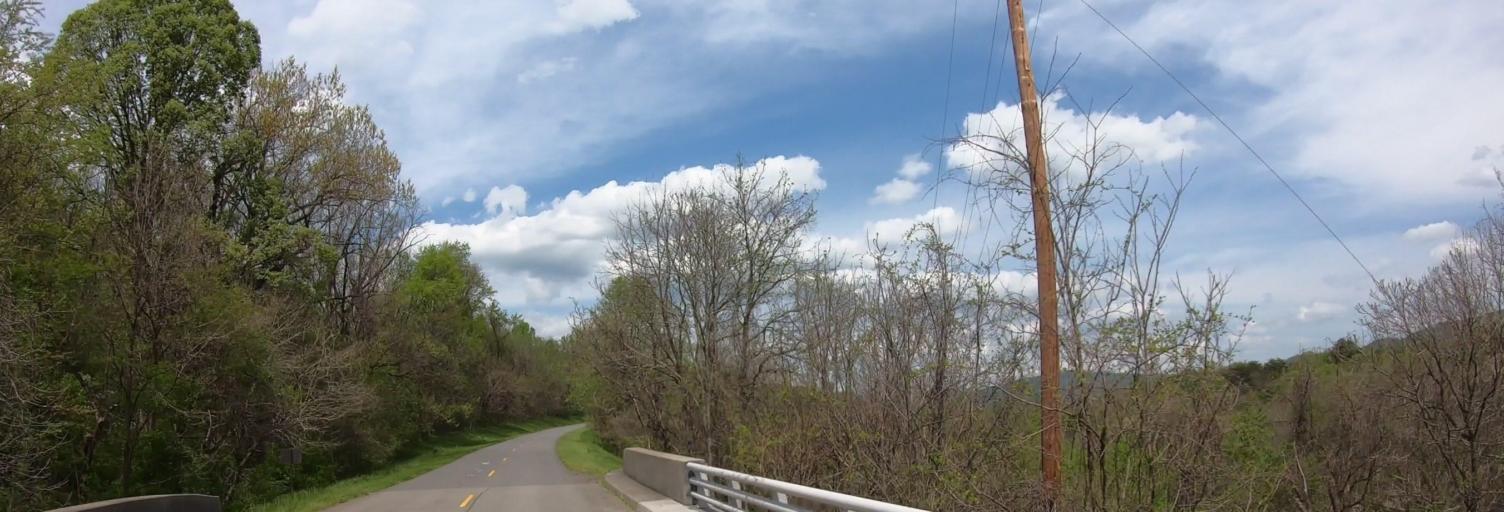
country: US
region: Virginia
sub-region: Botetourt County
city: Laymantown
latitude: 37.3366
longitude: -79.8513
